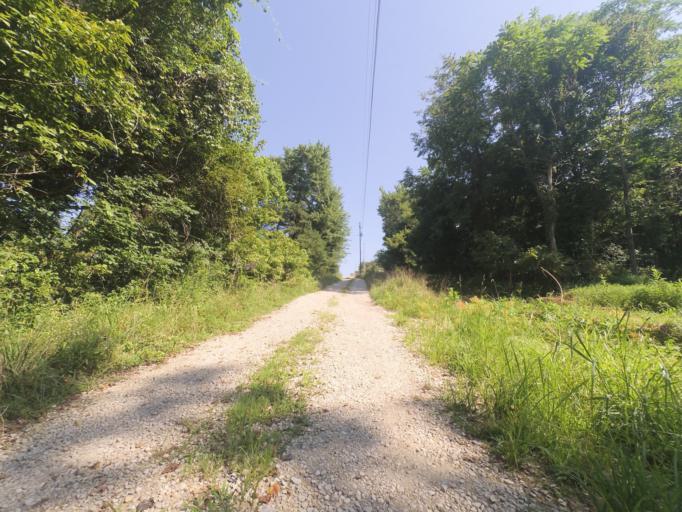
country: US
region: West Virginia
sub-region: Cabell County
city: Huntington
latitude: 38.4336
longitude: -82.4364
